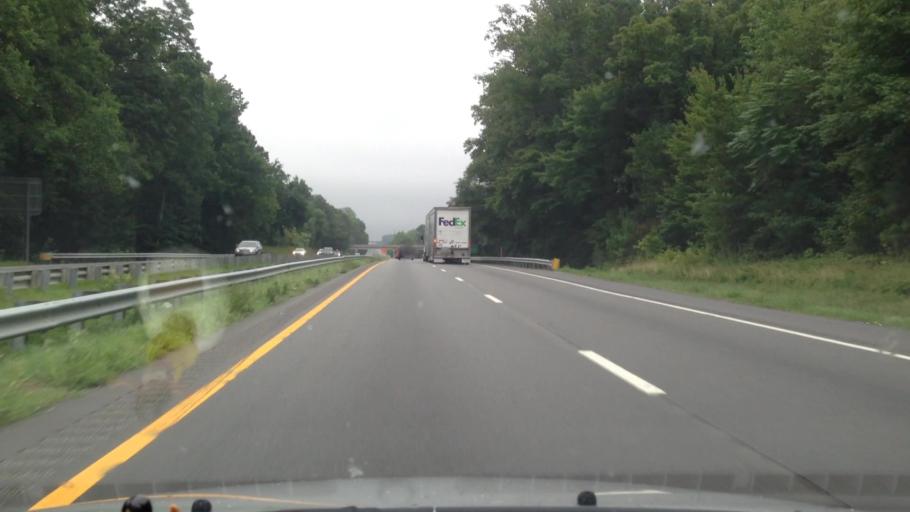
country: US
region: North Carolina
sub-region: Forsyth County
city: Kernersville
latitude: 36.1008
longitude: -80.0232
